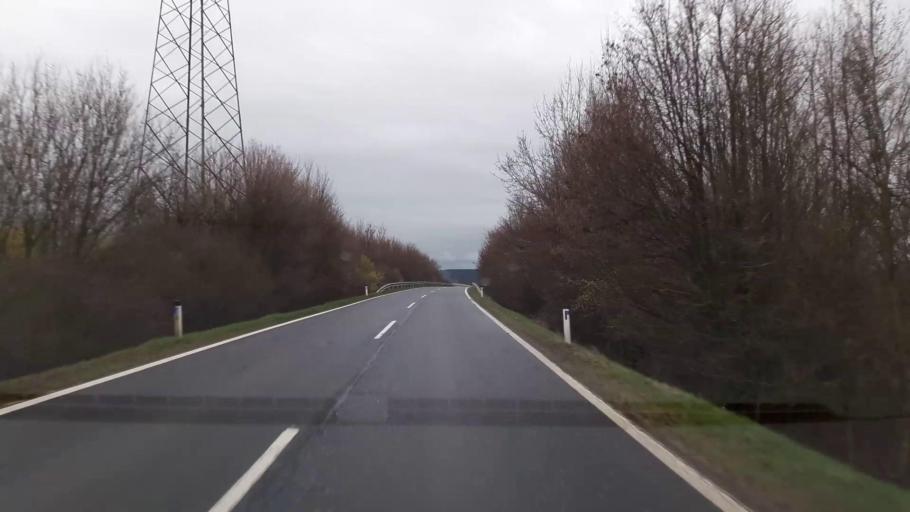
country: AT
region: Burgenland
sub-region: Politischer Bezirk Neusiedl am See
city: Bruckneudorf
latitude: 48.0440
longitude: 16.7858
